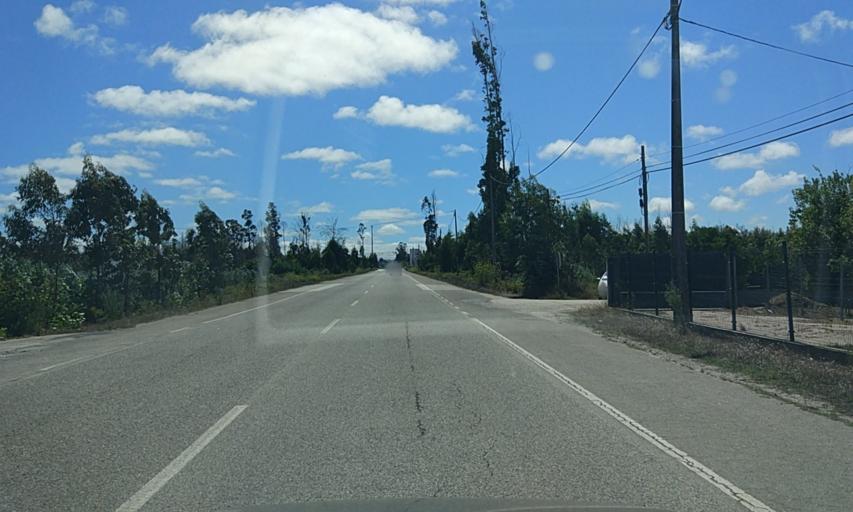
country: PT
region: Coimbra
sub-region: Mira
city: Mira
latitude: 40.3412
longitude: -8.7498
